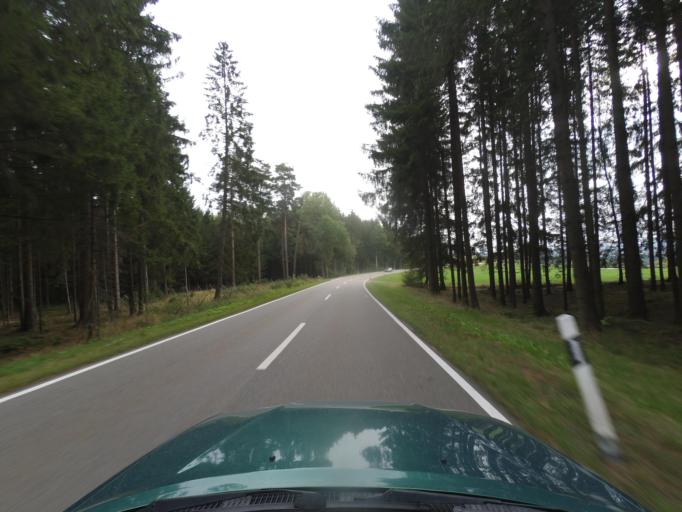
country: DE
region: Bavaria
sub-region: Upper Palatinate
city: Eslarn
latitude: 49.5865
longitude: 12.4818
